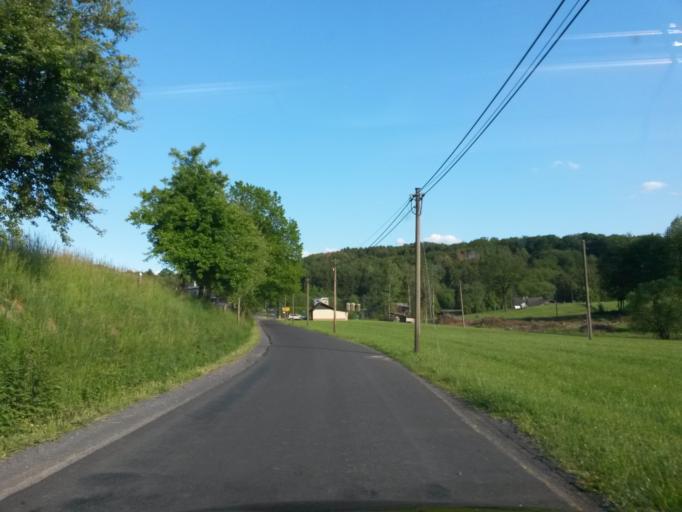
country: DE
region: North Rhine-Westphalia
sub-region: Regierungsbezirk Koln
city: Much
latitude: 50.8929
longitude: 7.3627
